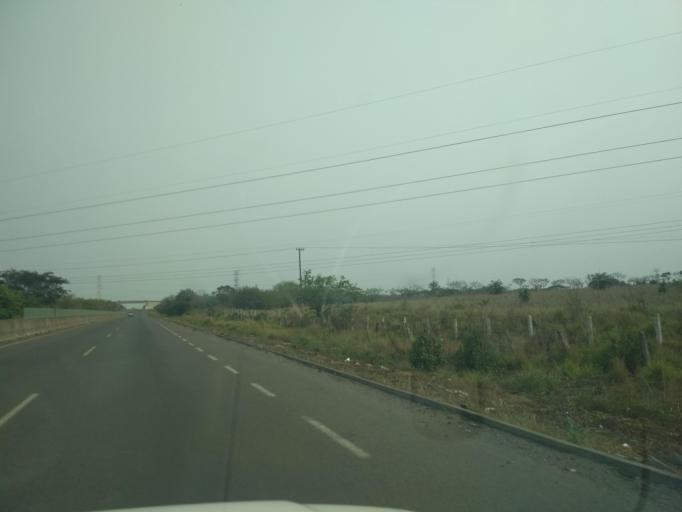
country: MX
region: Veracruz
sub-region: Veracruz
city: Las Amapolas
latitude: 19.1177
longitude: -96.2336
